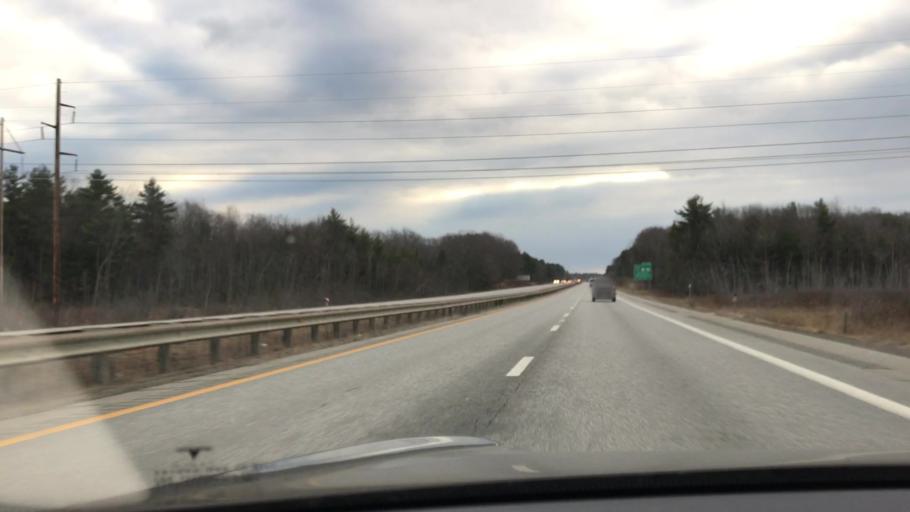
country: US
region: Maine
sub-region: Kennebec County
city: Hallowell
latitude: 44.2548
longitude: -69.8073
